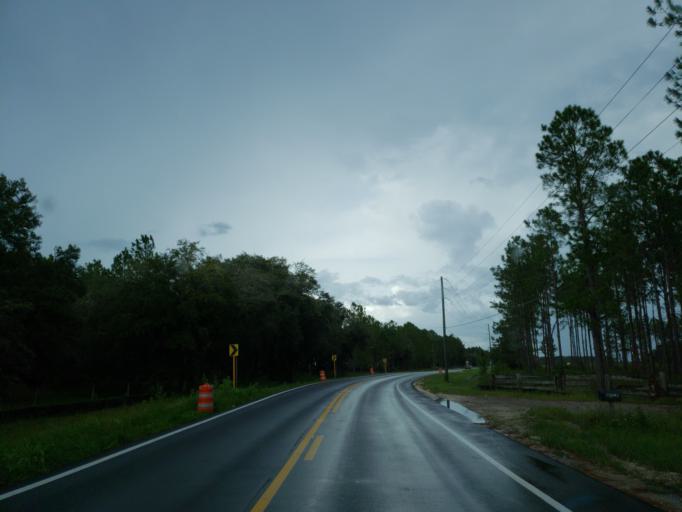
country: US
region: Florida
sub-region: Pasco County
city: Land O' Lakes
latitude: 28.3157
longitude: -82.4205
